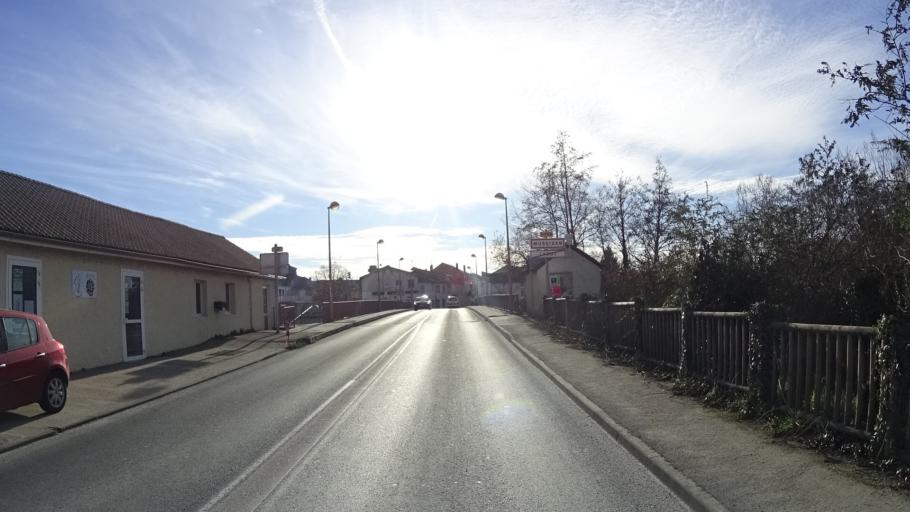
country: FR
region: Aquitaine
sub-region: Departement de la Dordogne
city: Mussidan
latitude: 45.0390
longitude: 0.3705
